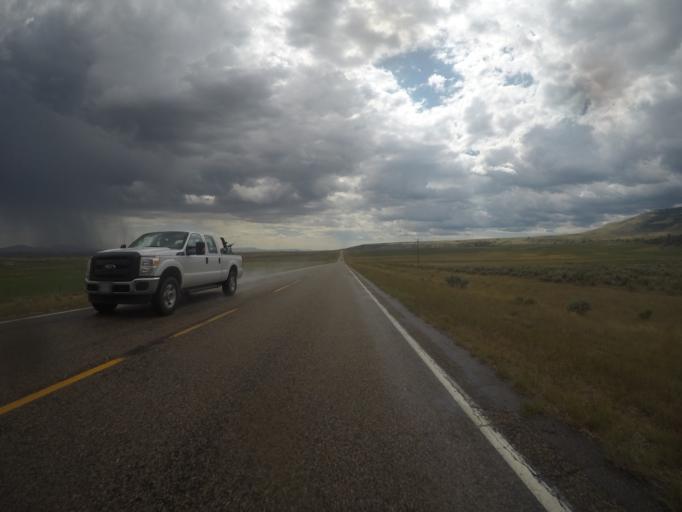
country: US
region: Utah
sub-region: Daggett County
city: Manila
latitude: 41.0234
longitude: -109.9109
